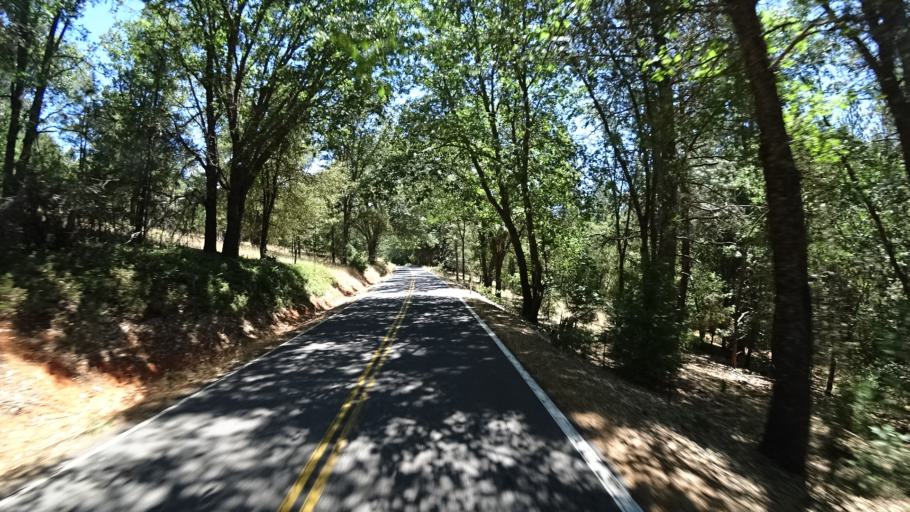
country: US
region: California
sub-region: Amador County
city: Pioneer
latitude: 38.3479
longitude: -120.5543
